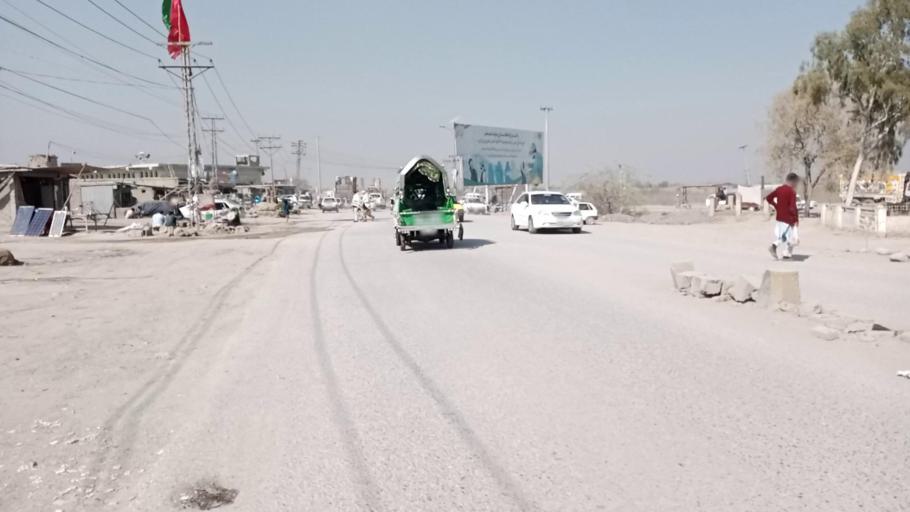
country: PK
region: Khyber Pakhtunkhwa
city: Peshawar
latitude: 33.9973
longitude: 71.4035
